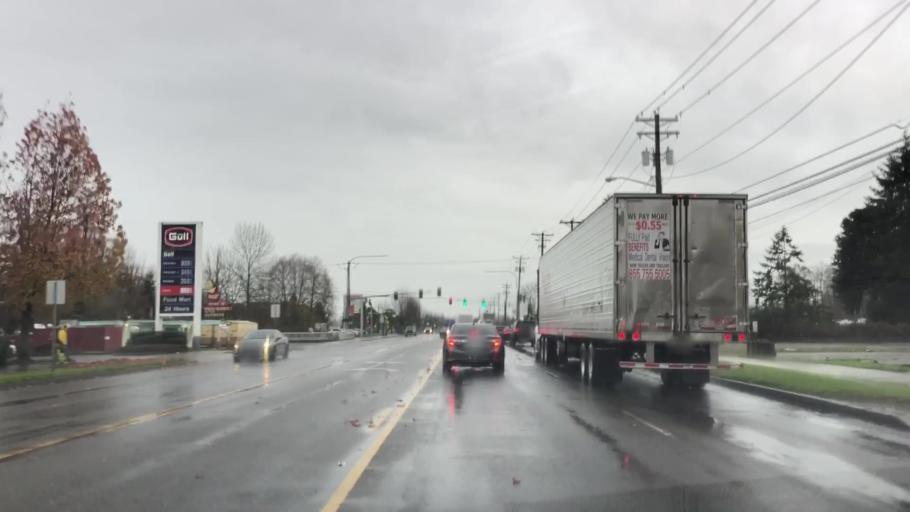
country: US
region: Washington
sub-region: Pierce County
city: Fife
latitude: 47.2430
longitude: -122.3712
